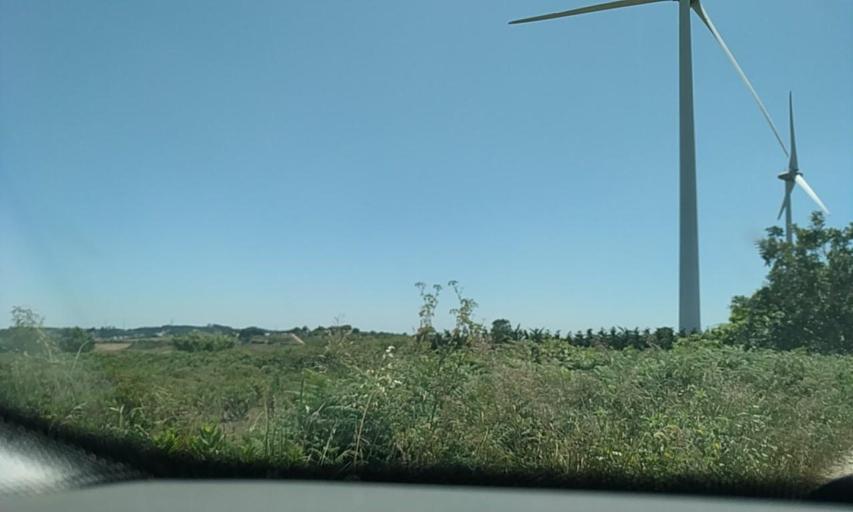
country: PT
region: Lisbon
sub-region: Sintra
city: Almargem
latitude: 38.8428
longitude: -9.2676
